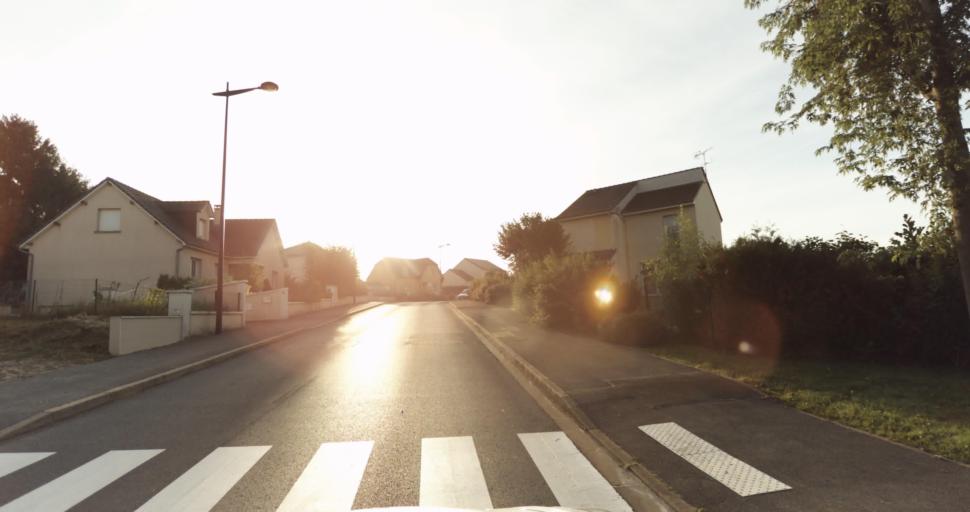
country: FR
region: Champagne-Ardenne
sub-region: Departement des Ardennes
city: Villers-Semeuse
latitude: 49.7407
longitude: 4.7402
